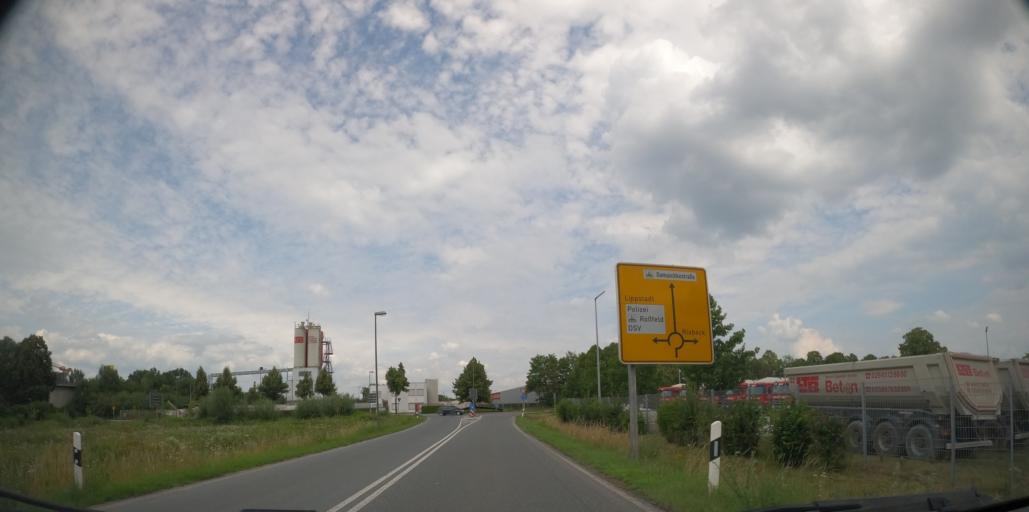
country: DE
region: North Rhine-Westphalia
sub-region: Regierungsbezirk Arnsberg
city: Lippstadt
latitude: 51.6700
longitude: 8.3697
